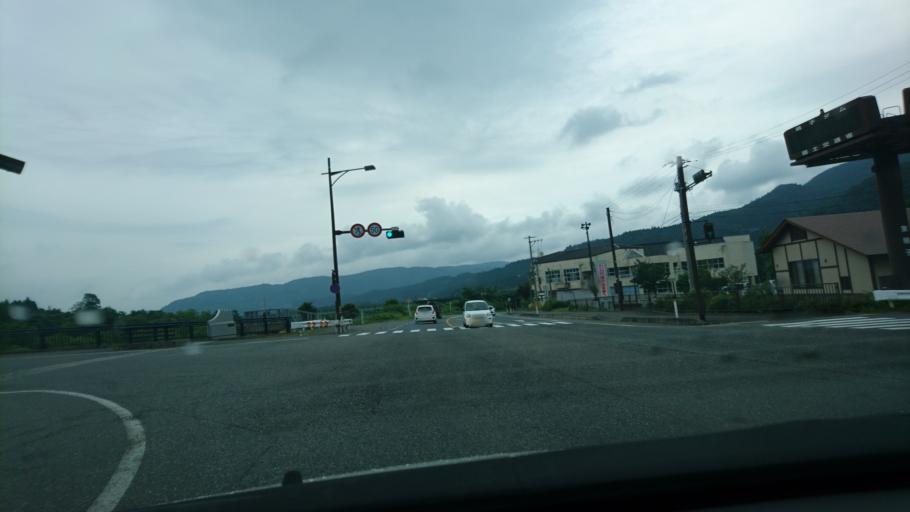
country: JP
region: Miyagi
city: Furukawa
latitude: 38.7462
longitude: 140.7375
